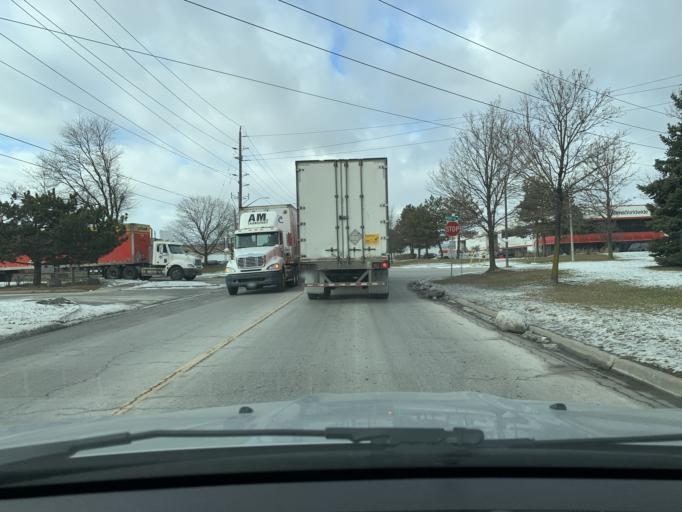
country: CA
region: Ontario
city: Brampton
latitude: 43.7281
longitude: -79.6814
